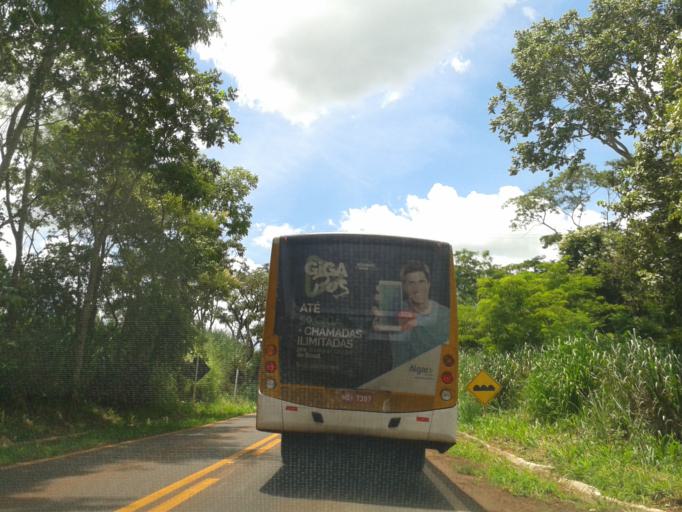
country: BR
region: Minas Gerais
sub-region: Ituiutaba
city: Ituiutaba
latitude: -18.9370
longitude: -49.4457
